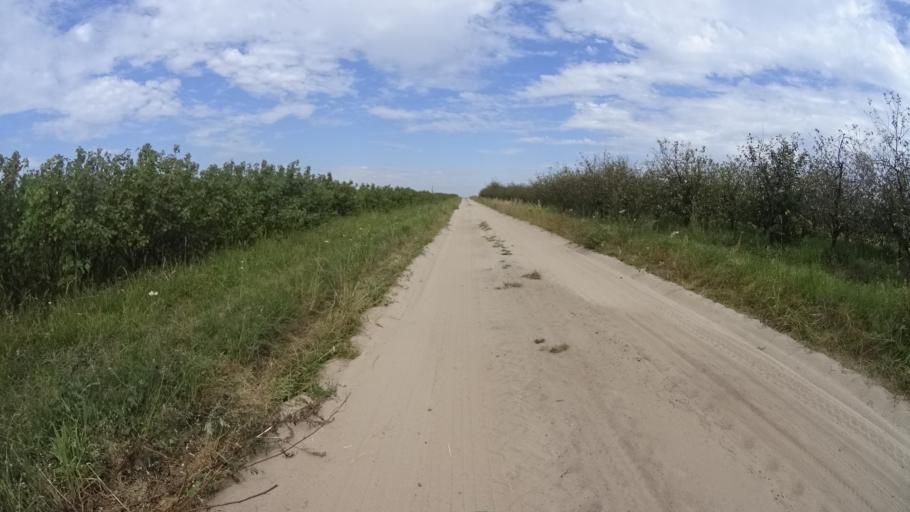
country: PL
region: Masovian Voivodeship
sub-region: Powiat bialobrzeski
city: Wysmierzyce
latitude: 51.6533
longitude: 20.7954
